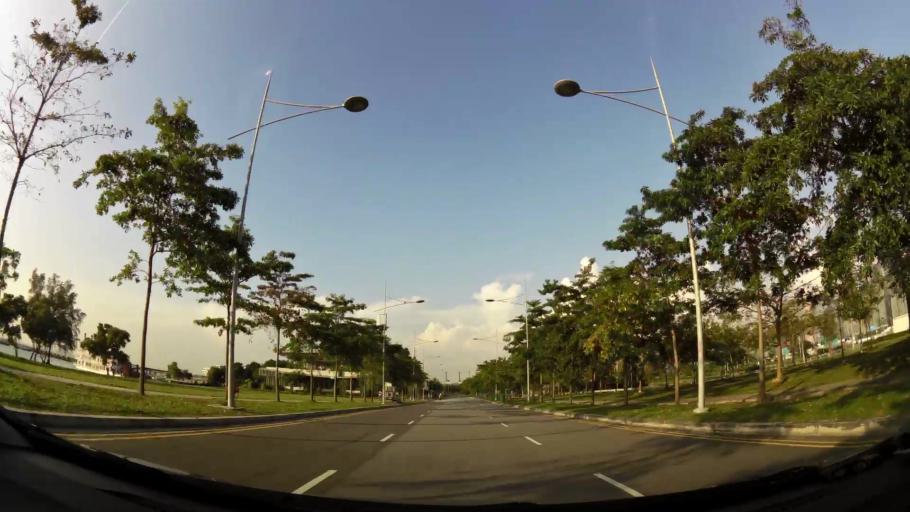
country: SG
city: Singapore
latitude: 1.2723
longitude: 103.8643
